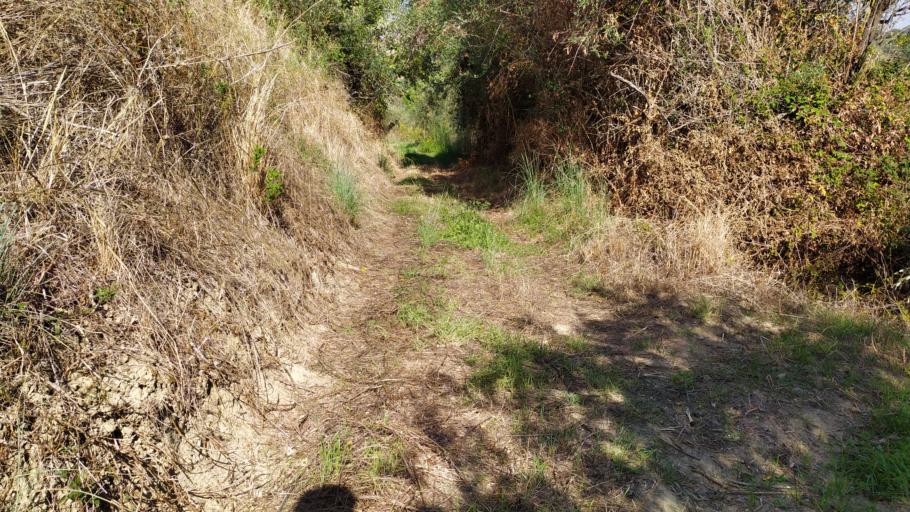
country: IT
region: Sicily
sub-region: Messina
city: Gualtieri Sicamino
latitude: 38.1595
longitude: 15.2984
